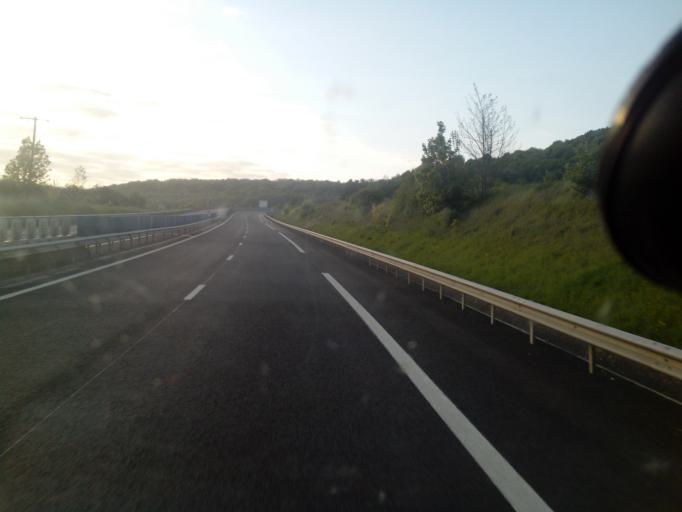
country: FR
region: Picardie
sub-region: Departement de la Somme
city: Bouttencourt
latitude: 49.9350
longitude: 1.6423
